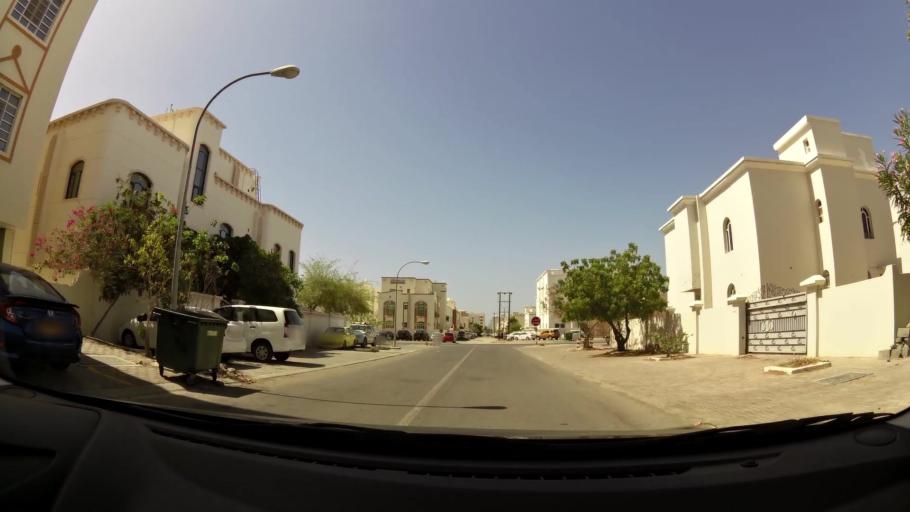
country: OM
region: Muhafazat Masqat
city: Bawshar
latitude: 23.5964
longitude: 58.3581
